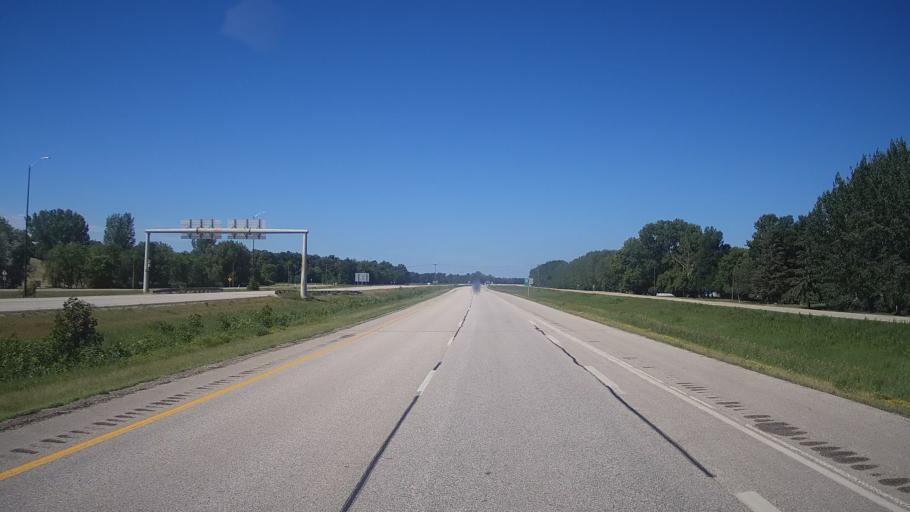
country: CA
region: Manitoba
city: Portage la Prairie
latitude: 49.9518
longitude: -98.2809
